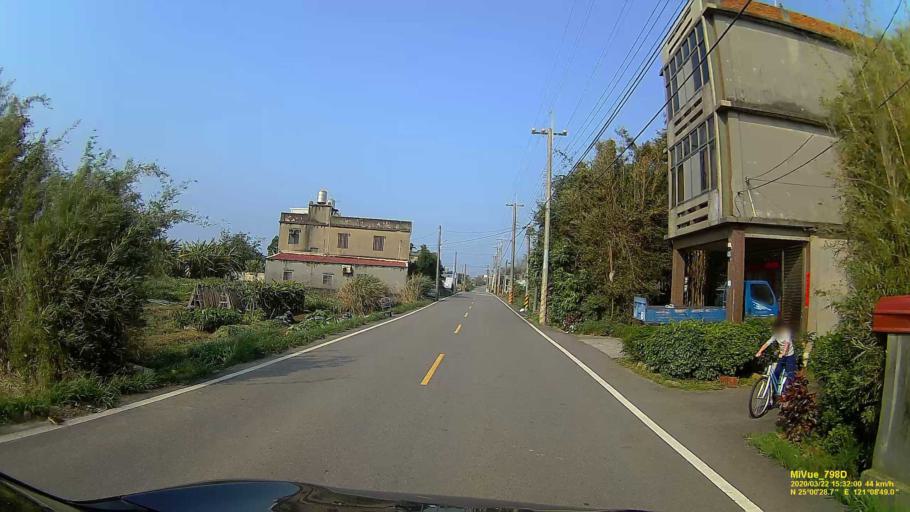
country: TW
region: Taiwan
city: Taoyuan City
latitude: 25.0082
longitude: 121.1472
